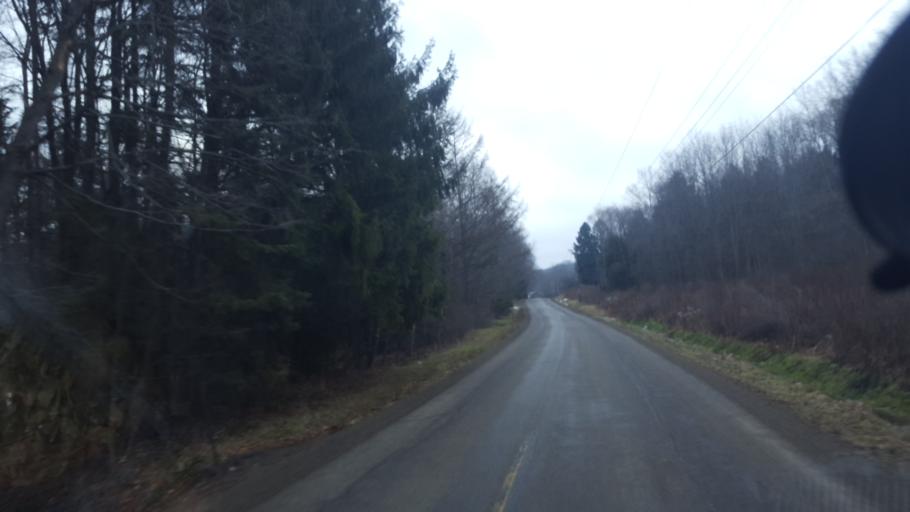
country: US
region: New York
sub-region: Allegany County
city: Andover
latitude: 41.9740
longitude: -77.7357
